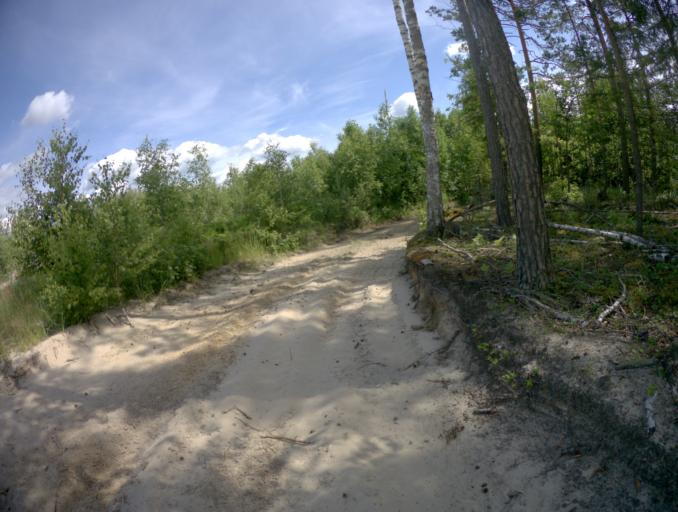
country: RU
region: Nizjnij Novgorod
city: Frolishchi
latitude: 56.4790
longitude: 42.5904
